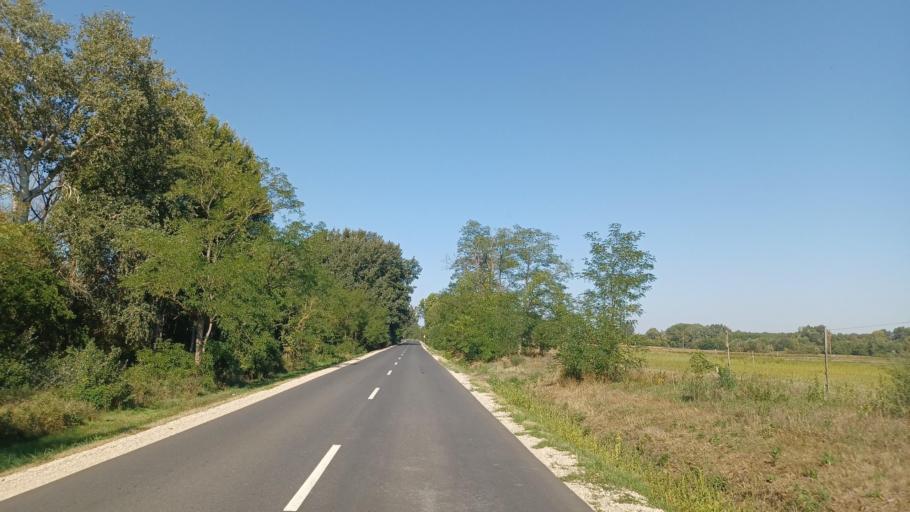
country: HU
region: Fejer
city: Alap
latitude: 46.7428
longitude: 18.6971
